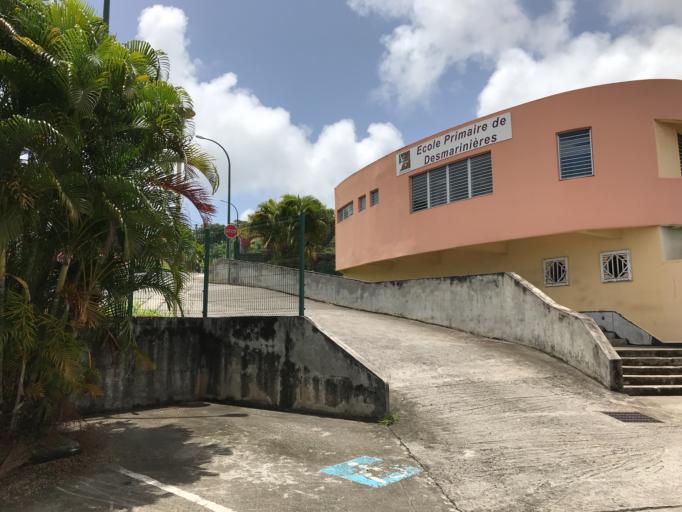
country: MQ
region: Martinique
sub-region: Martinique
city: Saint-Esprit
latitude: 14.5103
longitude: -60.9405
